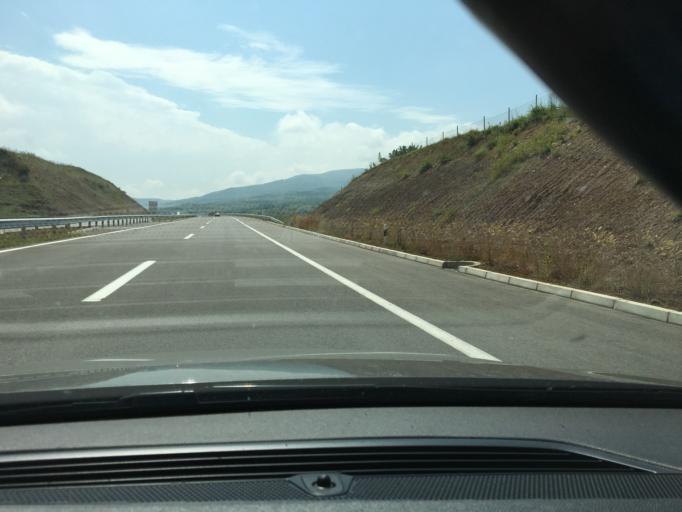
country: MK
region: Petrovec
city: Sredno Konjare
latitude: 41.9584
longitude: 21.7252
